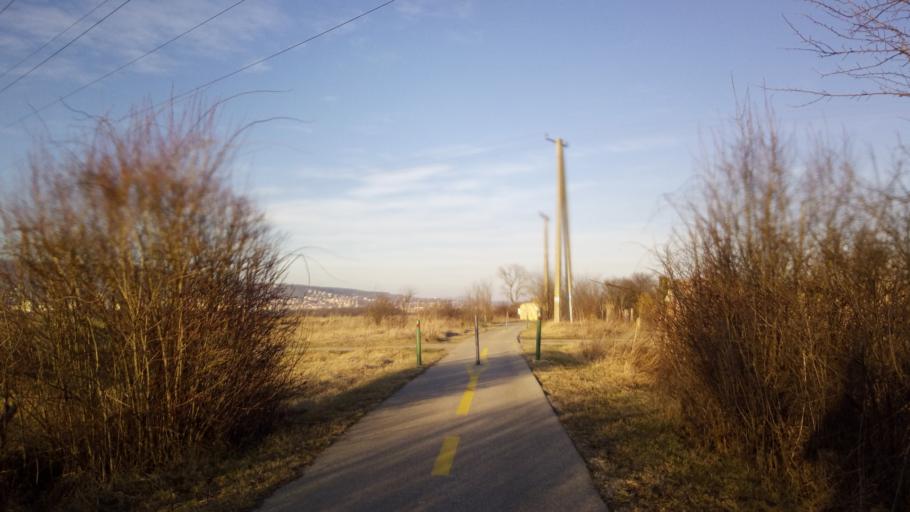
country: HU
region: Baranya
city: Pellerd
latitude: 46.0475
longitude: 18.1911
